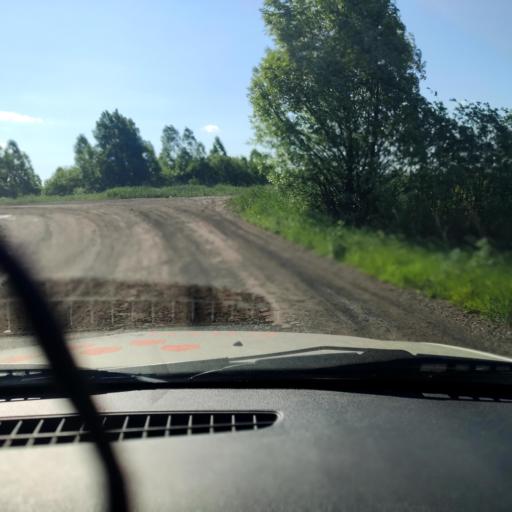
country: RU
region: Bashkortostan
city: Avdon
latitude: 54.5762
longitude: 55.8488
